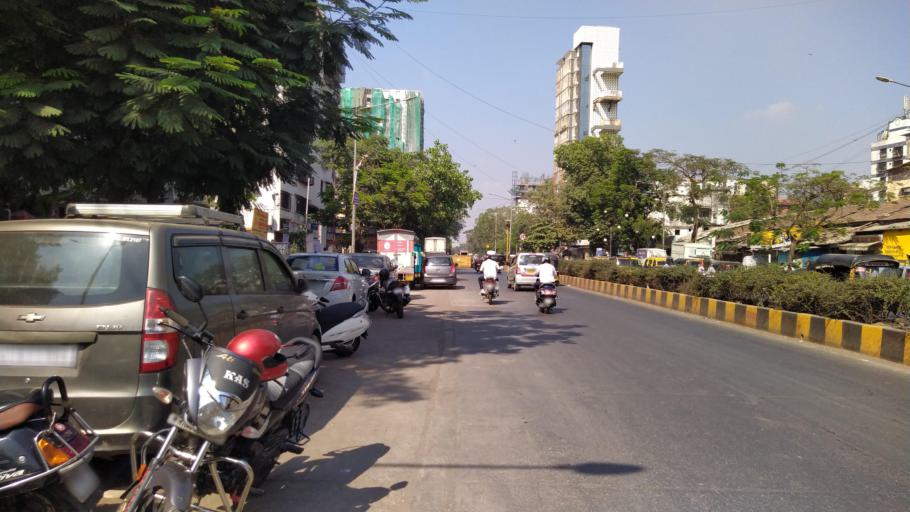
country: IN
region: Maharashtra
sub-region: Mumbai Suburban
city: Mumbai
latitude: 19.0652
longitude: 72.8745
